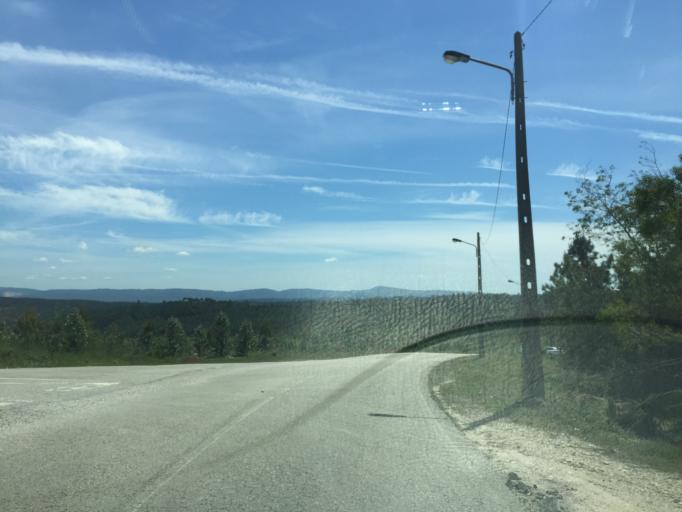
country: PT
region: Coimbra
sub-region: Soure
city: Soure
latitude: 40.0615
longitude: -8.6862
